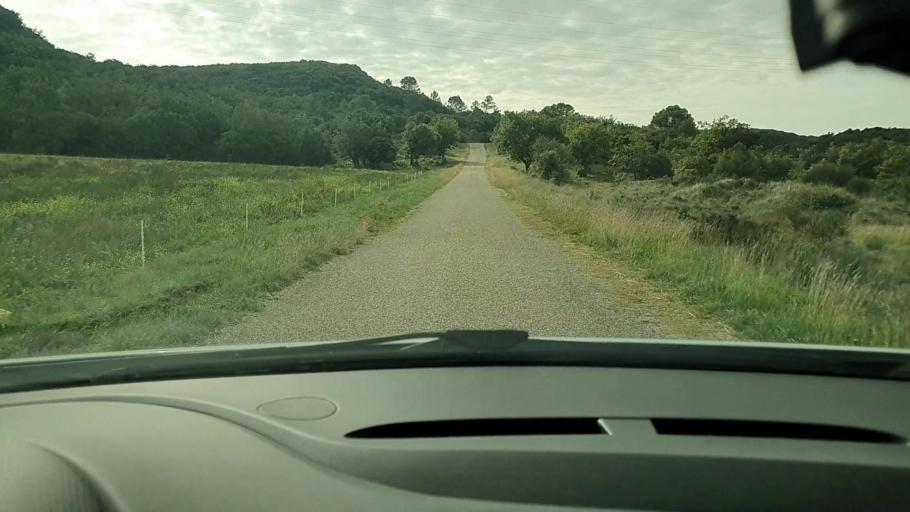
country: FR
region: Languedoc-Roussillon
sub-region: Departement du Gard
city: Montaren-et-Saint-Mediers
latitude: 44.0993
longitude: 4.3177
